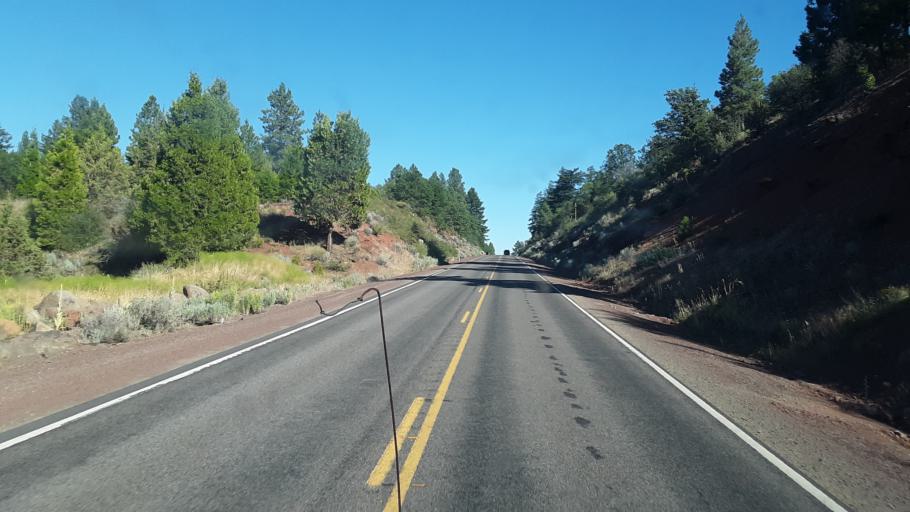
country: US
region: Oregon
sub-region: Klamath County
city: Klamath Falls
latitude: 42.2825
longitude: -121.9169
